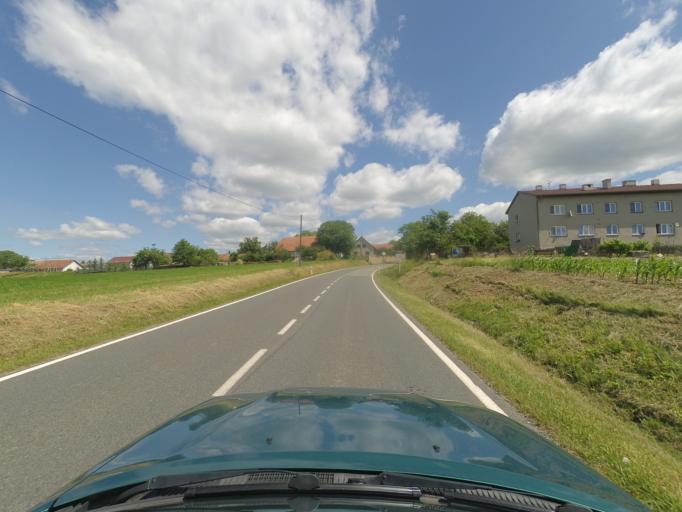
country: CZ
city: Dobruska
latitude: 50.3073
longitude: 16.1838
